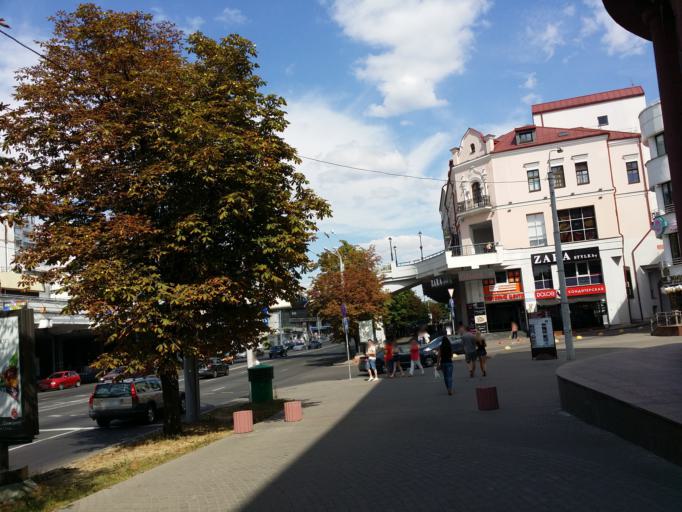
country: BY
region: Minsk
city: Minsk
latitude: 53.9033
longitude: 27.5509
